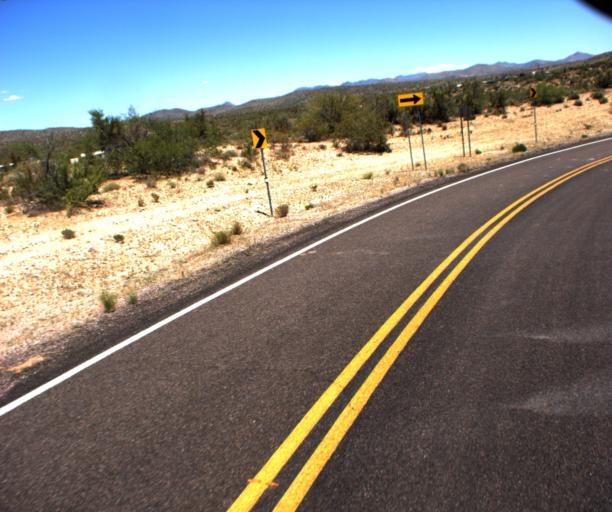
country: US
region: Arizona
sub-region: Yavapai County
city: Bagdad
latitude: 34.4841
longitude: -113.1883
